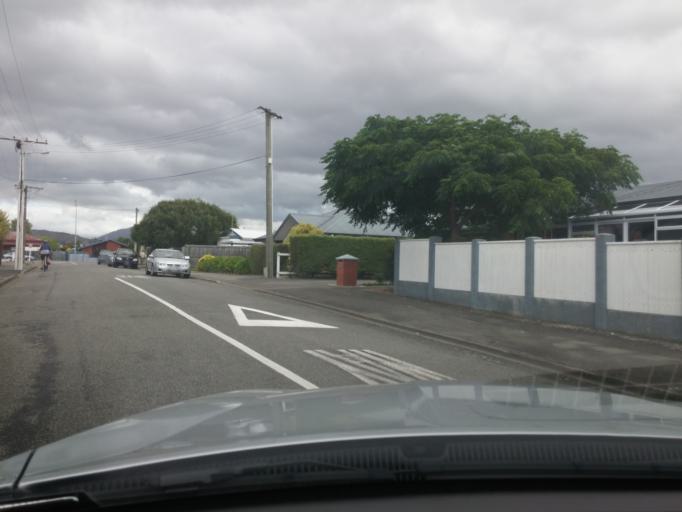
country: NZ
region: Marlborough
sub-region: Marlborough District
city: Blenheim
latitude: -41.5108
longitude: 173.9503
